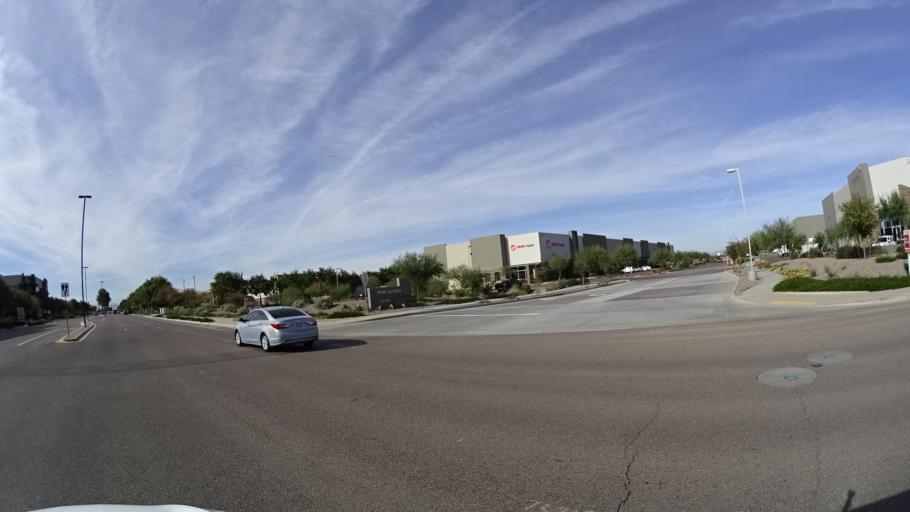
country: US
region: Arizona
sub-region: Maricopa County
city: Chandler
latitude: 33.2775
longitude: -111.7834
